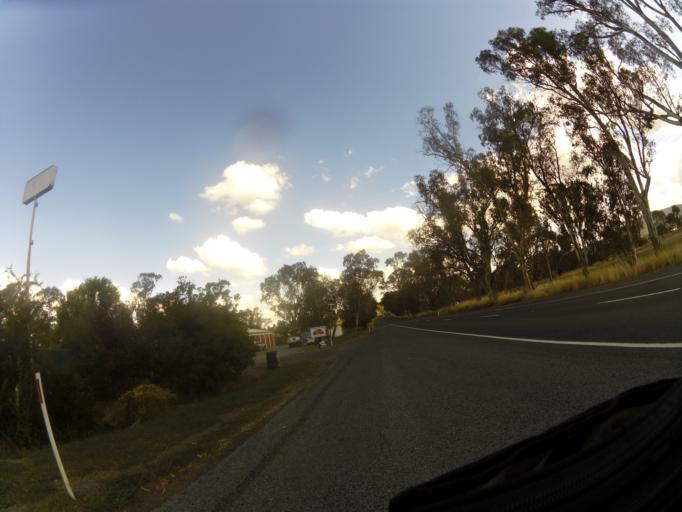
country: AU
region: Victoria
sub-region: Mansfield
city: Mansfield
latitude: -36.9334
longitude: 146.0000
